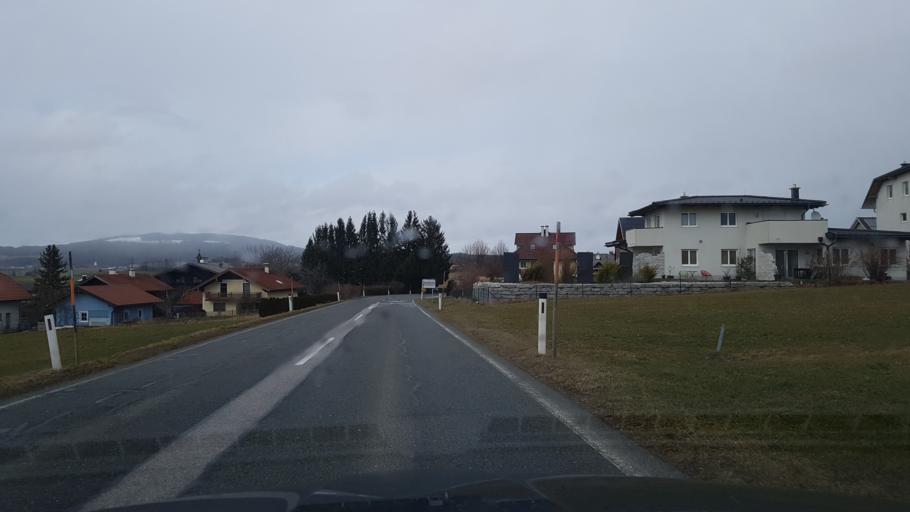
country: AT
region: Salzburg
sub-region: Politischer Bezirk Salzburg-Umgebung
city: Neumarkt am Wallersee
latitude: 47.9307
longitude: 13.2208
